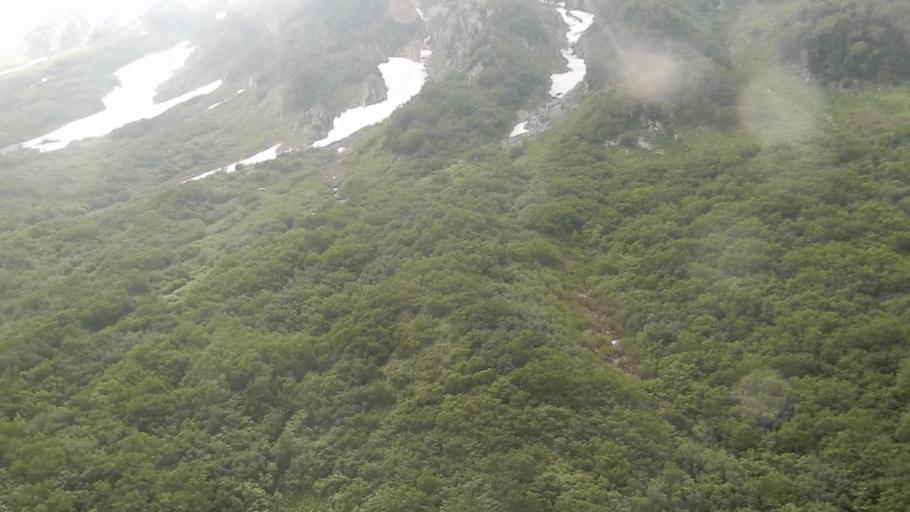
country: JP
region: Nagano
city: Omachi
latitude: 36.5682
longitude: 137.6393
